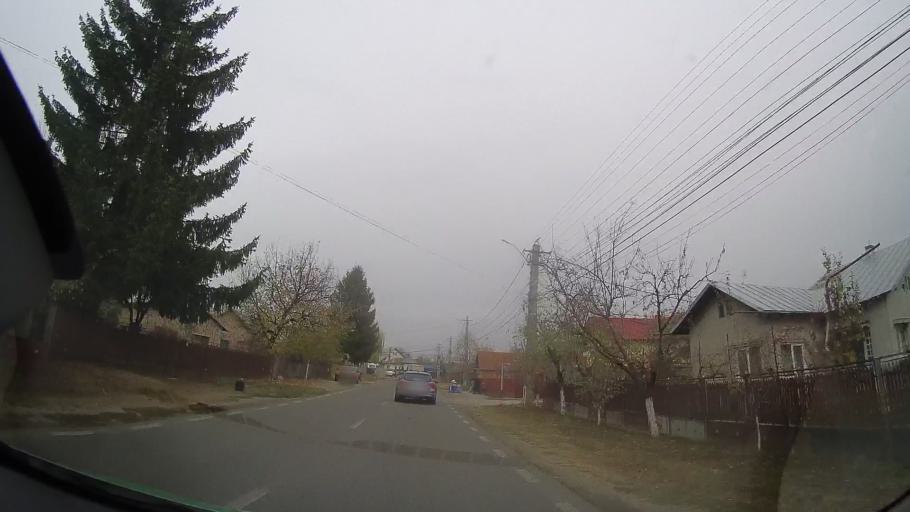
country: RO
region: Prahova
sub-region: Oras Baicoi
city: Liliesti
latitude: 45.0299
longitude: 25.8870
